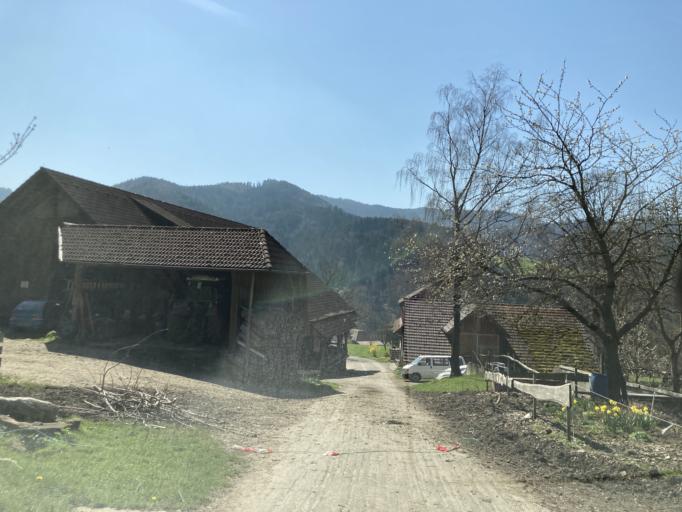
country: DE
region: Baden-Wuerttemberg
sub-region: Freiburg Region
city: Glottertal
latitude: 48.0514
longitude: 7.9725
